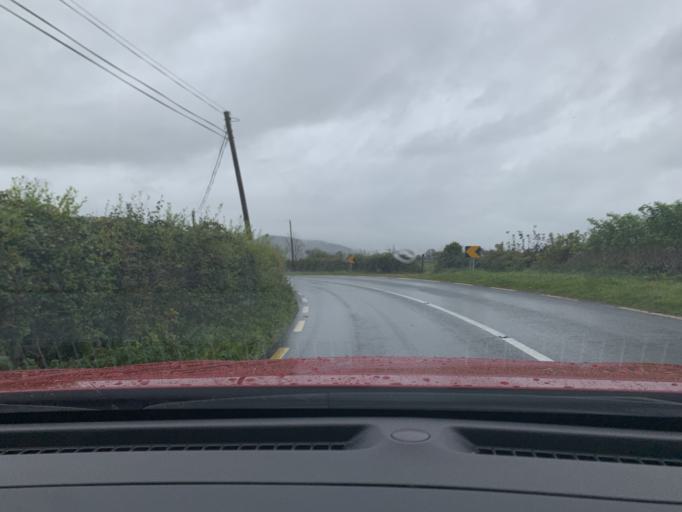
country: IE
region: Connaught
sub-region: Sligo
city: Sligo
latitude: 54.3087
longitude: -8.4335
